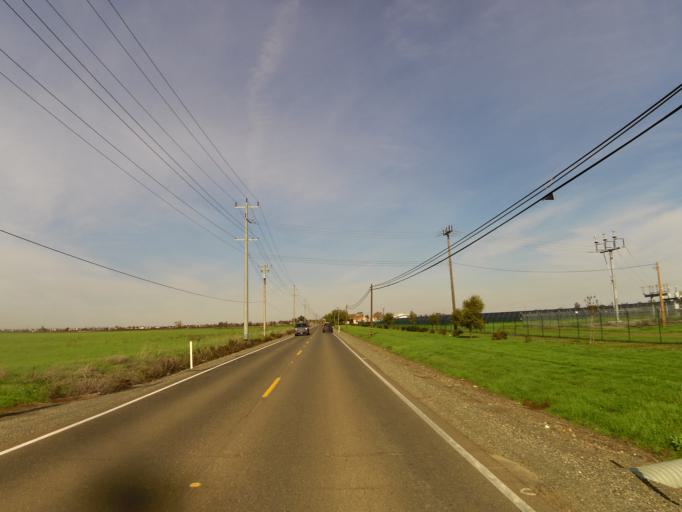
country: US
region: California
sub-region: Sacramento County
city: Laguna
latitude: 38.3649
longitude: -121.4175
